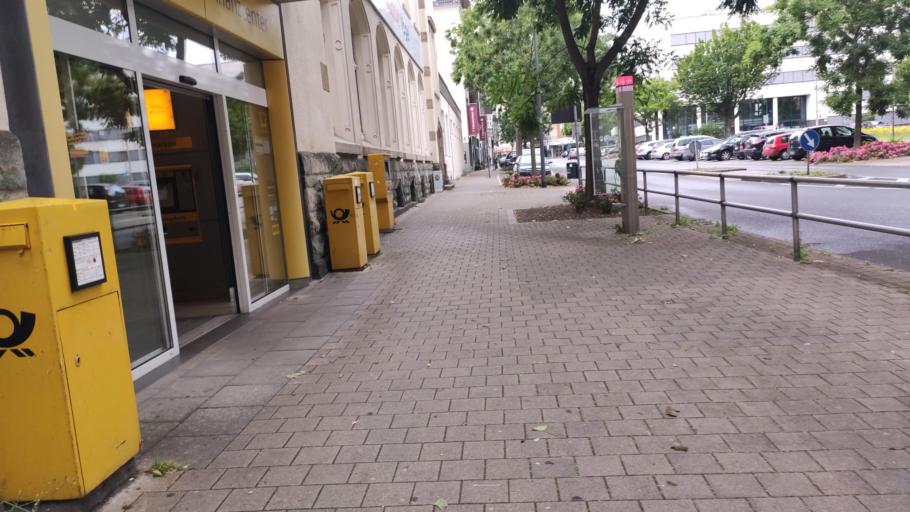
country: DE
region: North Rhine-Westphalia
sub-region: Regierungsbezirk Arnsberg
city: Herne
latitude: 51.5394
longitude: 7.2200
